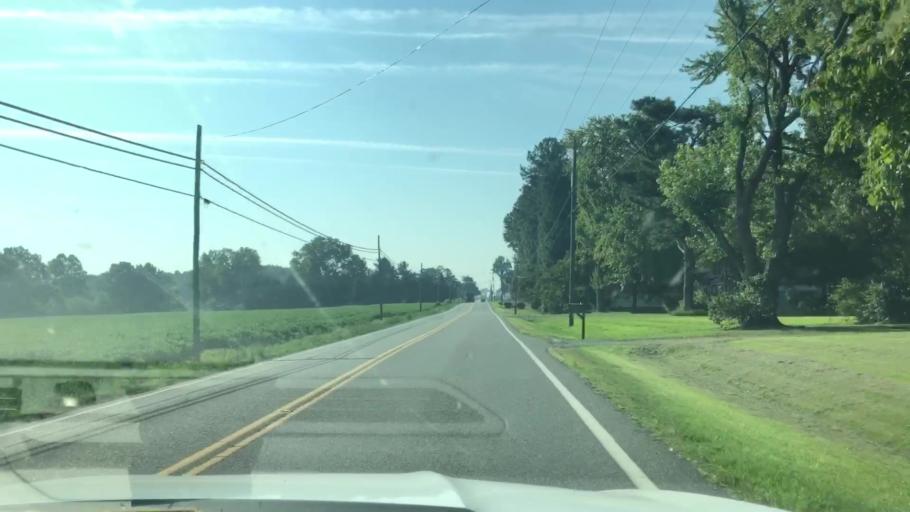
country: US
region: Virginia
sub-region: Richmond County
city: Warsaw
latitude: 37.8952
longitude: -76.6749
